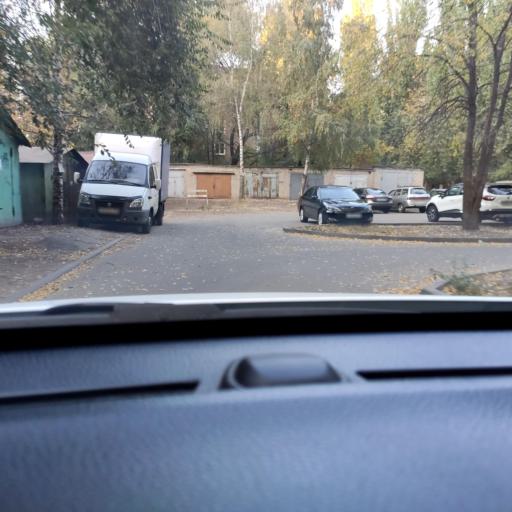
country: RU
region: Voronezj
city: Voronezh
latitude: 51.6477
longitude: 39.2357
